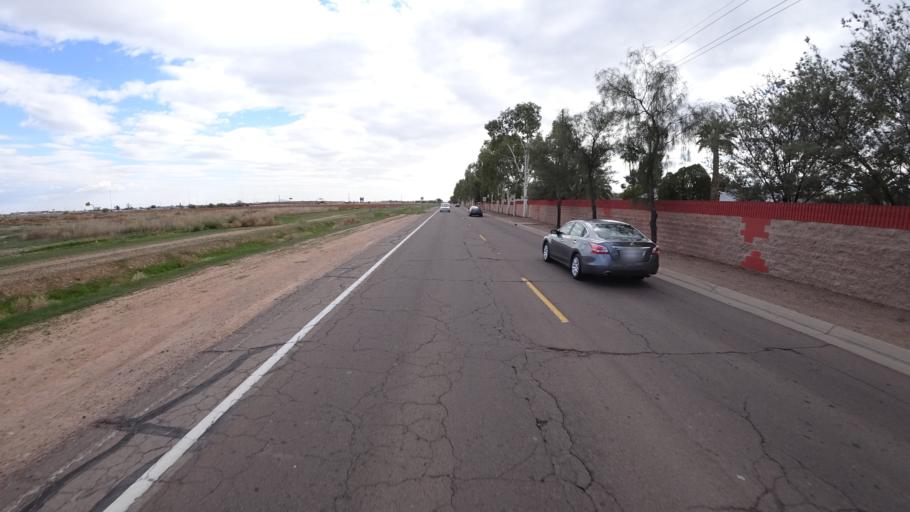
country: US
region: Arizona
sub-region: Maricopa County
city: Scottsdale
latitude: 33.5029
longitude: -111.8917
